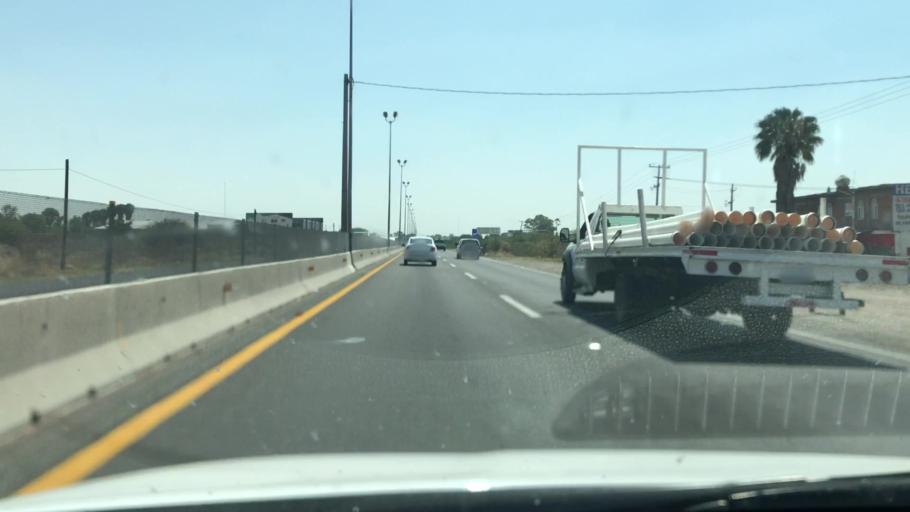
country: MX
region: Guanajuato
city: Abasolo
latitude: 20.4533
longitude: -101.5453
